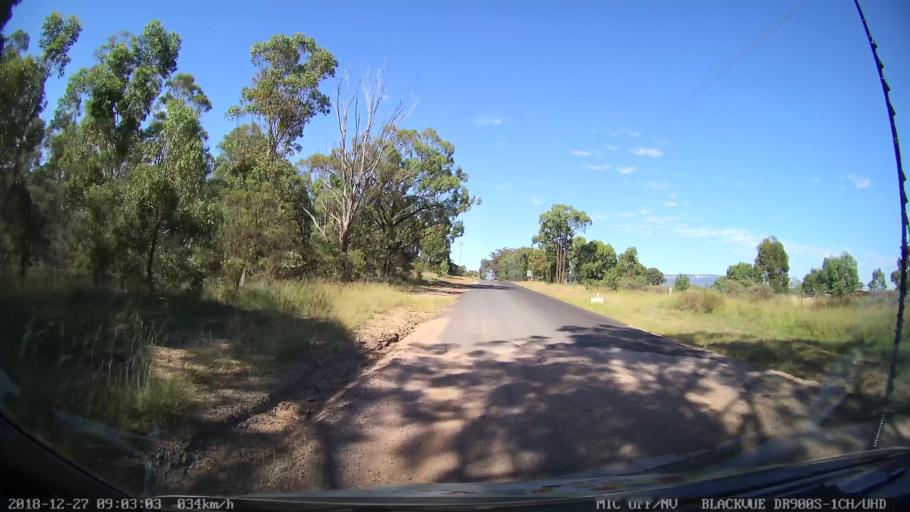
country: AU
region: New South Wales
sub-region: Lithgow
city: Portland
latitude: -33.1039
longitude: 150.2053
